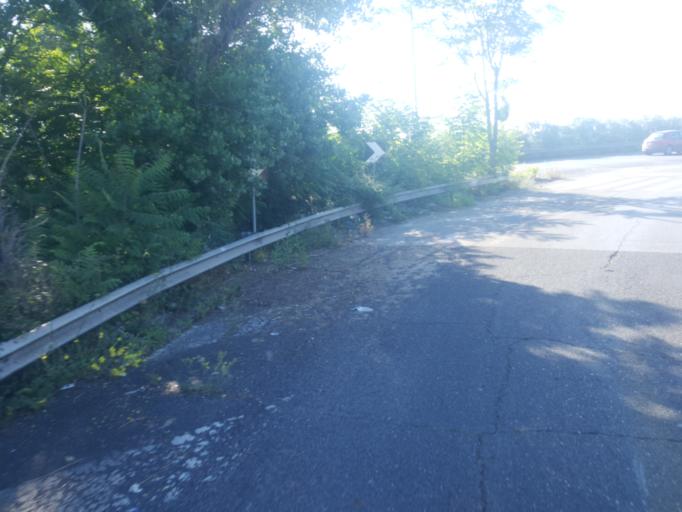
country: IT
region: Latium
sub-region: Citta metropolitana di Roma Capitale
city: Frascati
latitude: 41.8624
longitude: 12.6268
